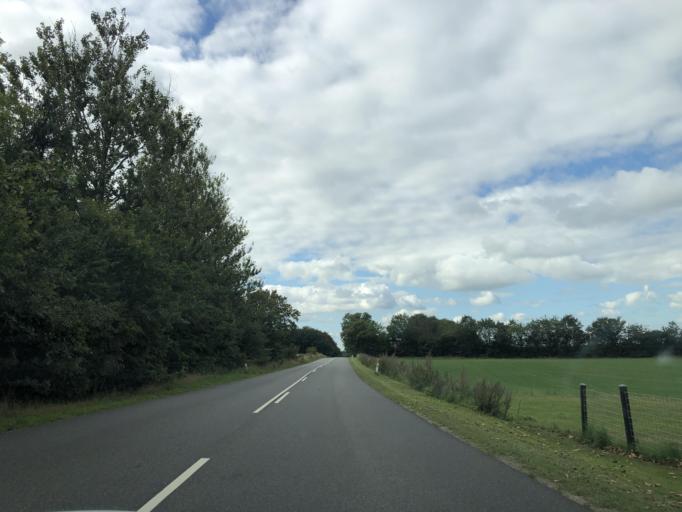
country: DK
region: North Denmark
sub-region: Rebild Kommune
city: Stovring
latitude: 56.8719
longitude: 9.7280
